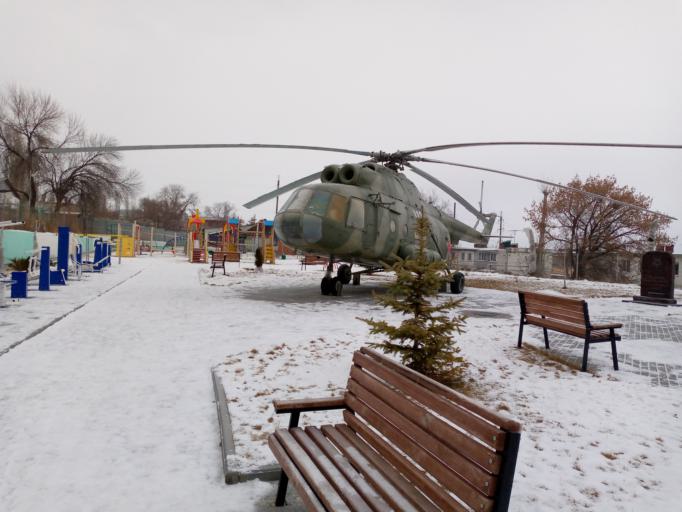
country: RU
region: Saratov
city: Sokolovyy
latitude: 51.3609
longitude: 45.8330
